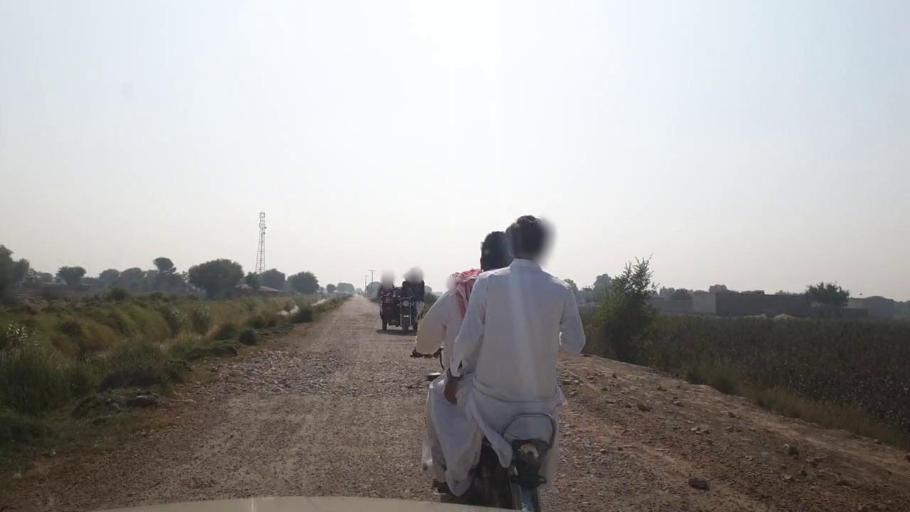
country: PK
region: Sindh
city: Bhan
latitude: 26.5309
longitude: 67.7776
